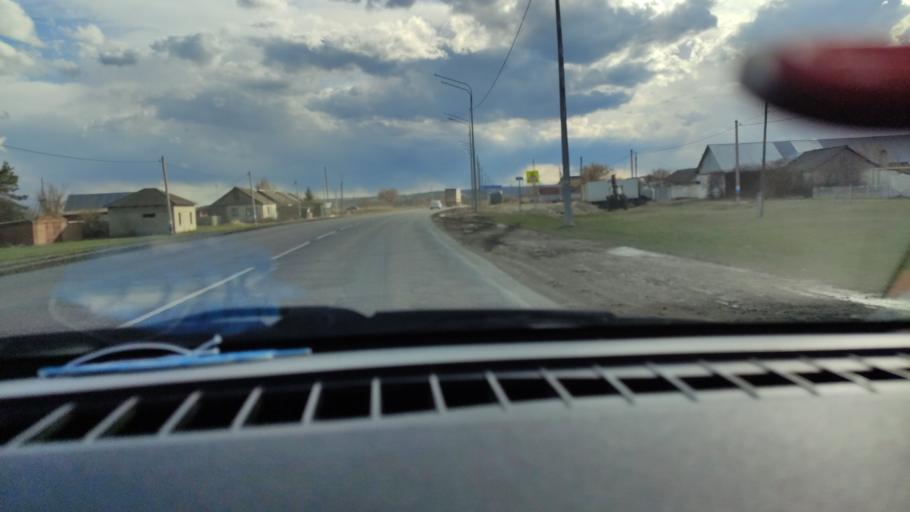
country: RU
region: Saratov
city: Sinodskoye
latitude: 51.9810
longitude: 46.6567
